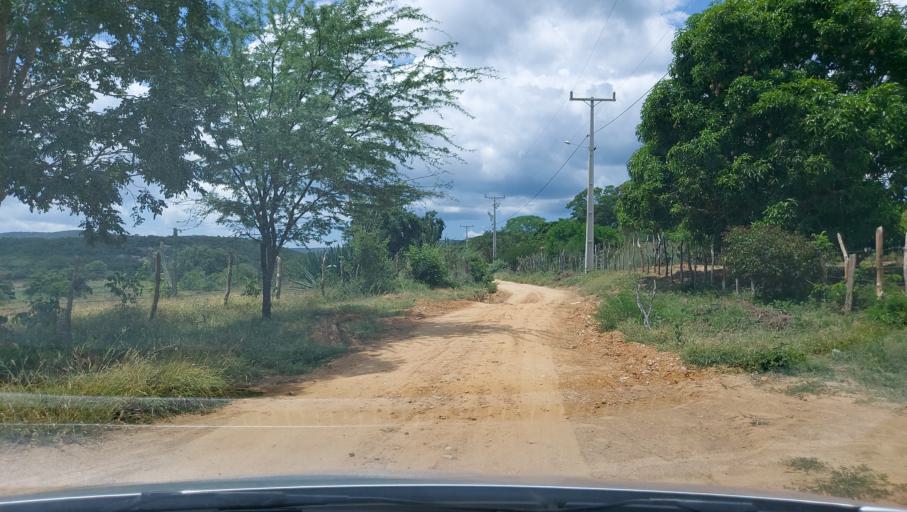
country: BR
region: Bahia
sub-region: Oliveira Dos Brejinhos
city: Beira Rio
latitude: -12.0194
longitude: -42.6312
